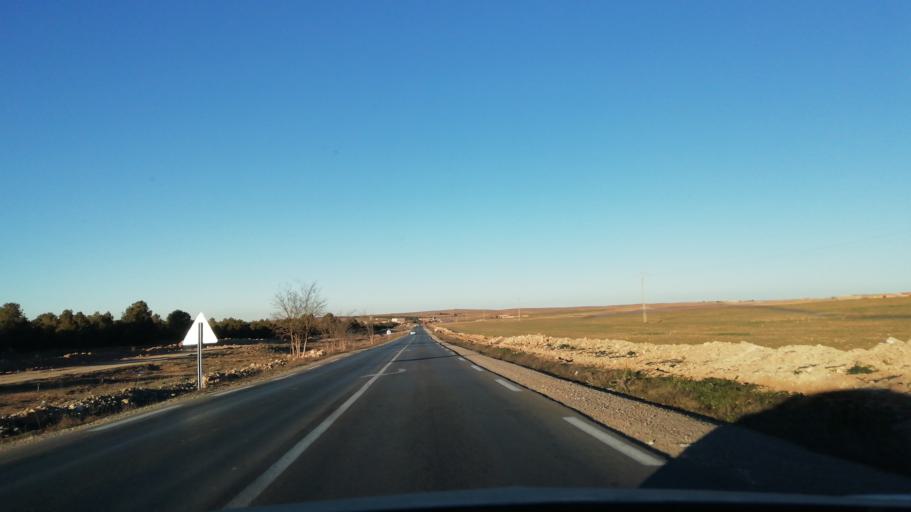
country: DZ
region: Saida
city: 'Ain el Hadjar
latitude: 34.5635
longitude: 0.1203
